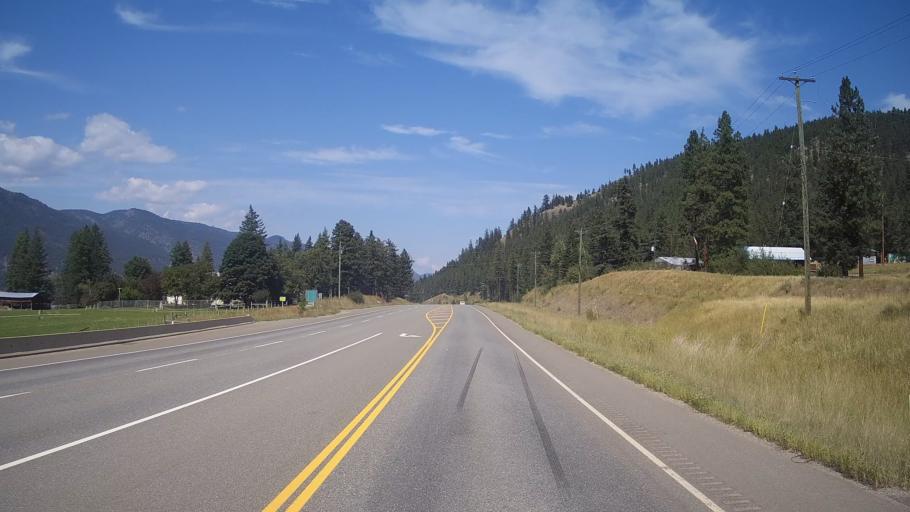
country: CA
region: British Columbia
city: Kamloops
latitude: 51.0128
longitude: -120.2219
